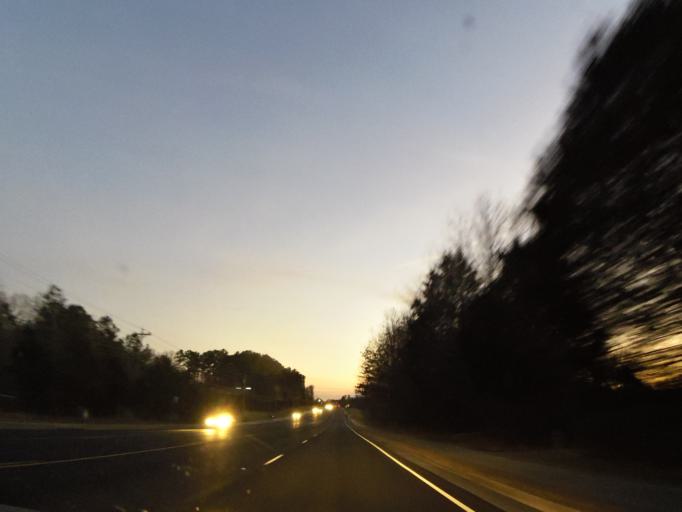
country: US
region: Georgia
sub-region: Whitfield County
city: Varnell
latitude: 34.8689
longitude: -84.9445
